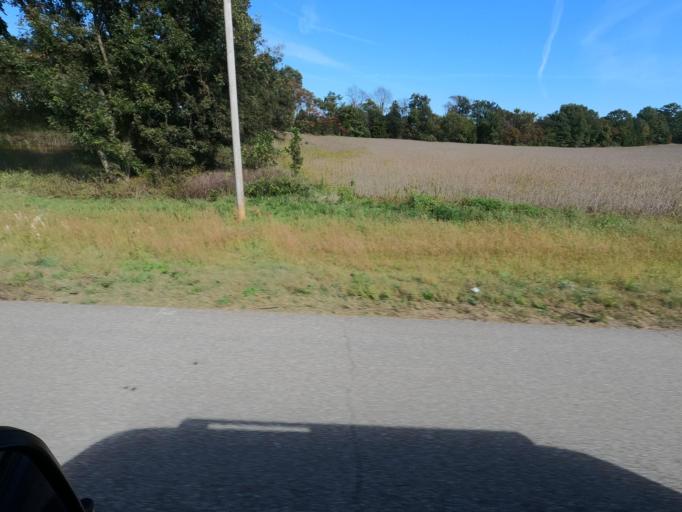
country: US
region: Tennessee
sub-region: Lauderdale County
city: Halls
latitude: 35.8938
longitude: -89.2393
